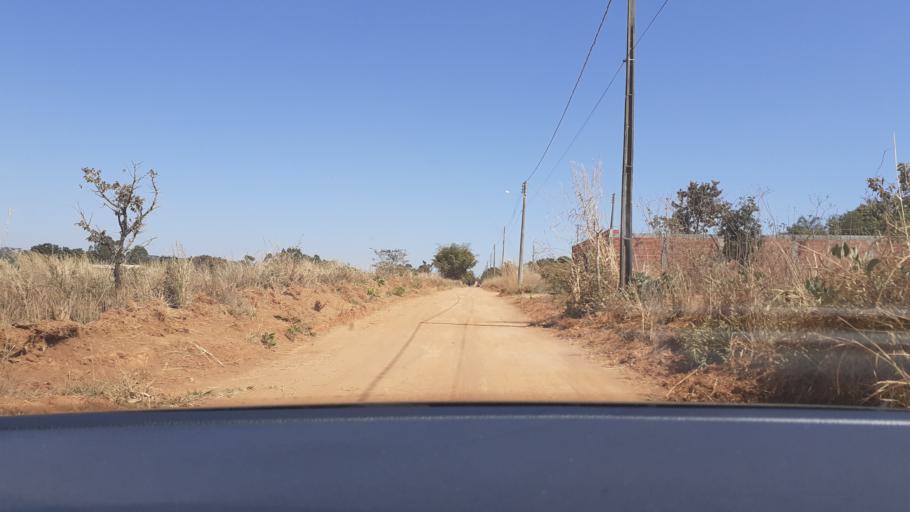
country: BR
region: Goias
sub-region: Aparecida De Goiania
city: Aparecida de Goiania
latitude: -16.8712
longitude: -49.2754
